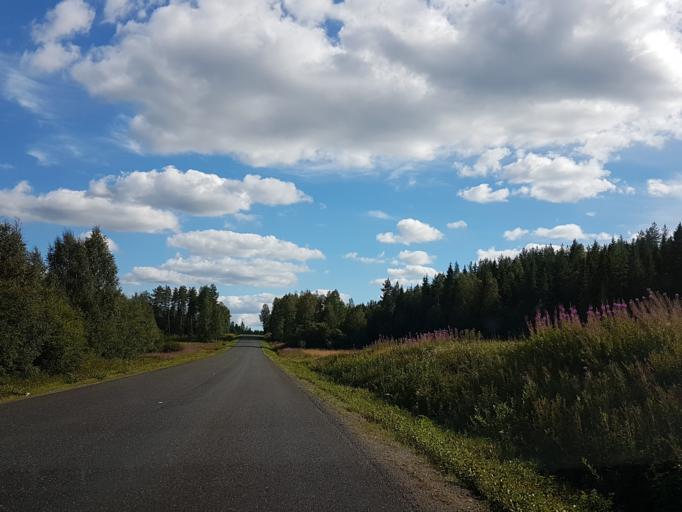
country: SE
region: Vaesterbotten
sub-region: Skelleftea Kommun
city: Burtraesk
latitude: 64.2912
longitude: 20.5235
